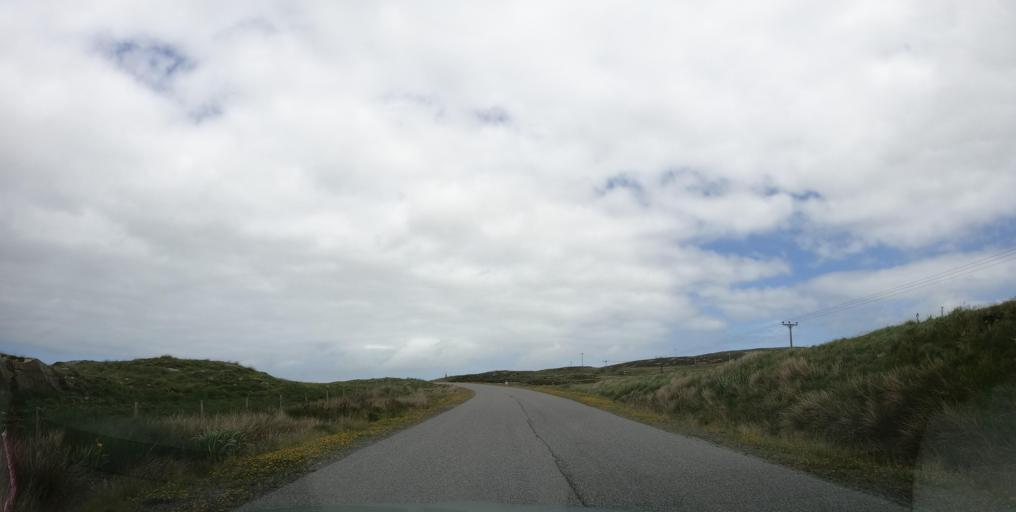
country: GB
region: Scotland
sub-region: Eilean Siar
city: Isle of South Uist
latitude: 57.2297
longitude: -7.3971
